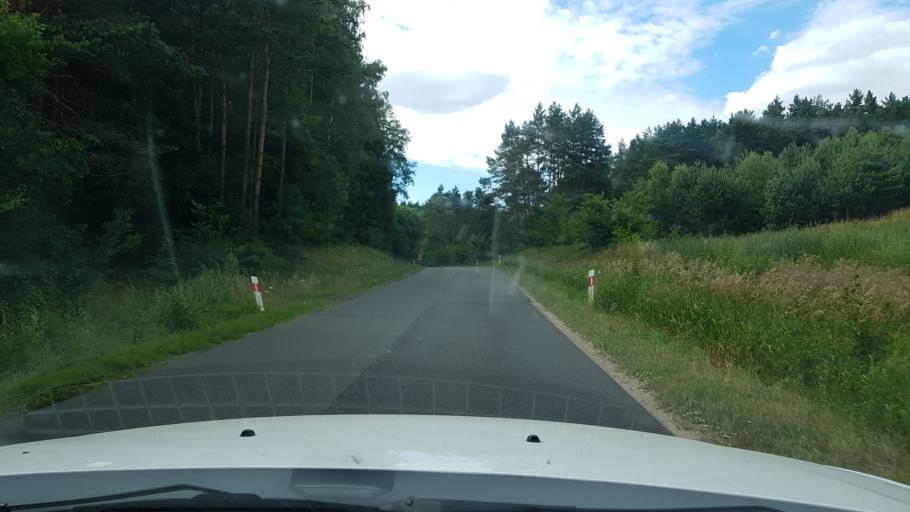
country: PL
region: West Pomeranian Voivodeship
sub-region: Powiat drawski
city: Zlocieniec
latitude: 53.4882
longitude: 16.0412
